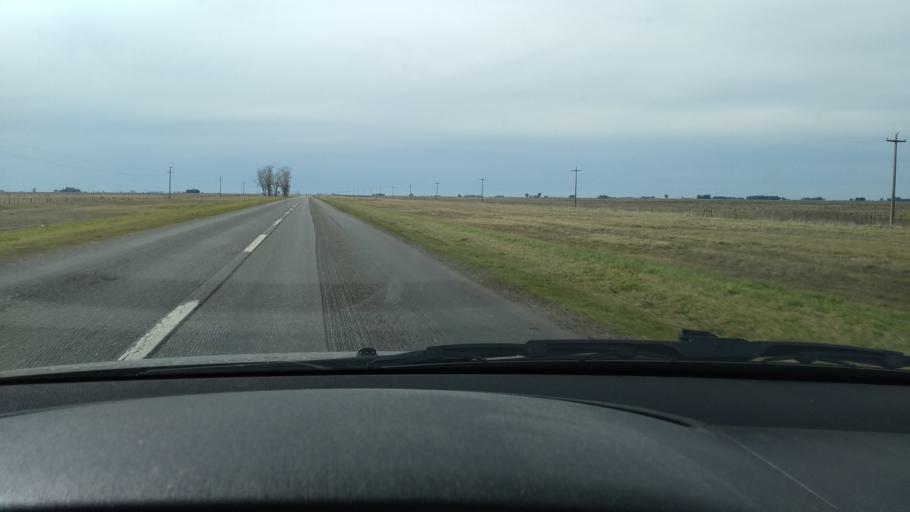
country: AR
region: Buenos Aires
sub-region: Partido de Azul
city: Azul
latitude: -36.7052
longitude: -59.7557
